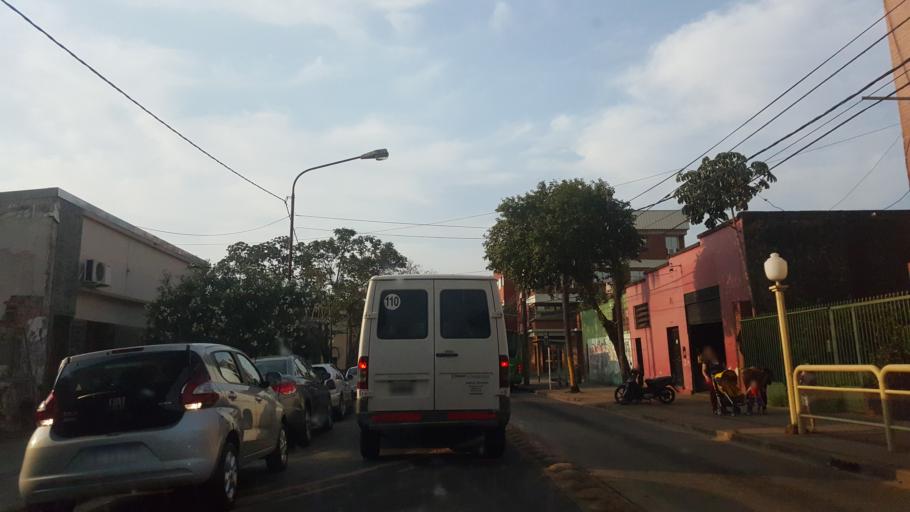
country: AR
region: Misiones
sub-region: Departamento de Capital
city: Posadas
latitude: -27.3626
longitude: -55.8962
